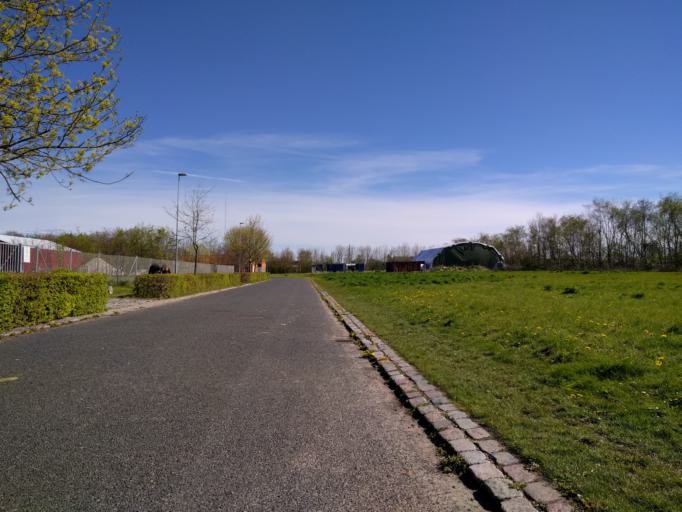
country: DK
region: South Denmark
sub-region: Kerteminde Kommune
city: Munkebo
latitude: 55.4633
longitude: 10.5421
